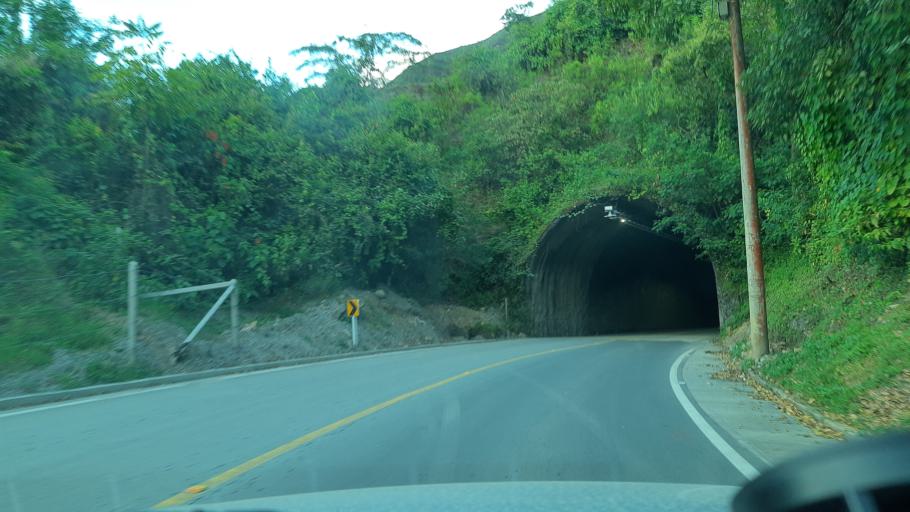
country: CO
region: Boyaca
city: Somondoco
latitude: 4.9970
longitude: -73.3524
